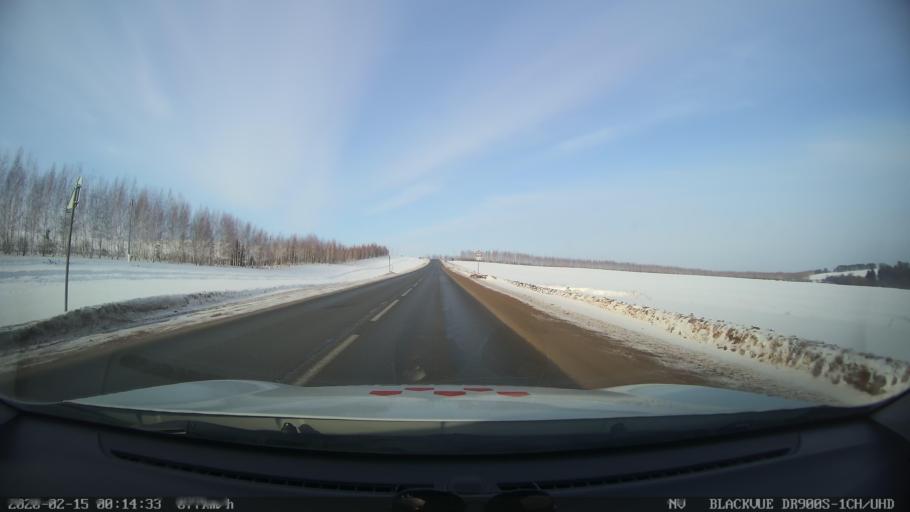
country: RU
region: Tatarstan
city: Stolbishchi
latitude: 55.4871
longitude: 49.0044
